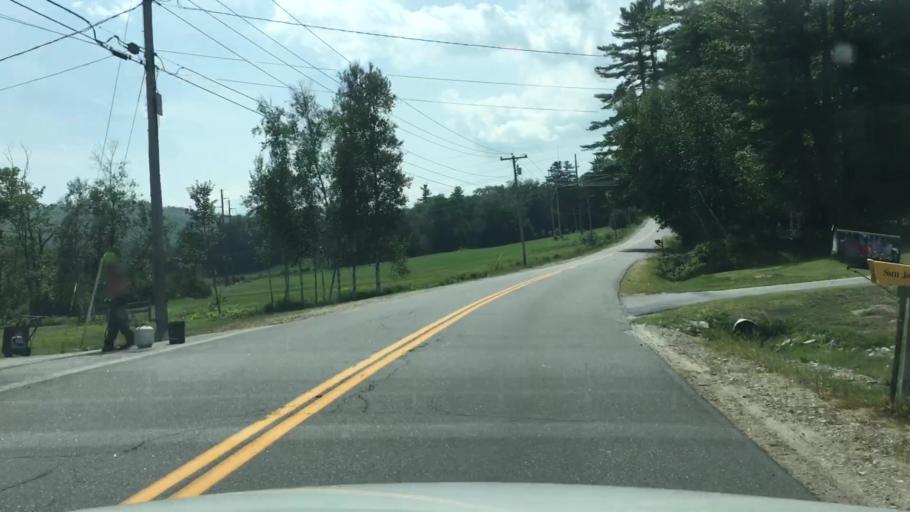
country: US
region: Maine
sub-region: Oxford County
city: Rumford
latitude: 44.5239
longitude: -70.5118
